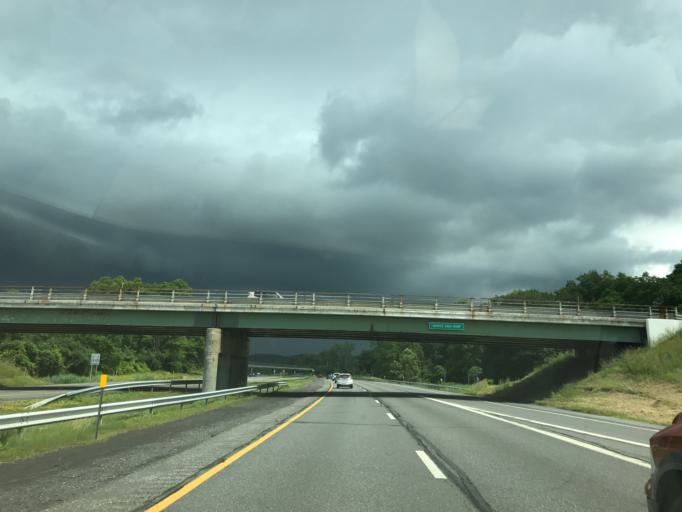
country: US
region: New York
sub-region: Albany County
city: Ravena
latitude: 42.4292
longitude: -73.8039
